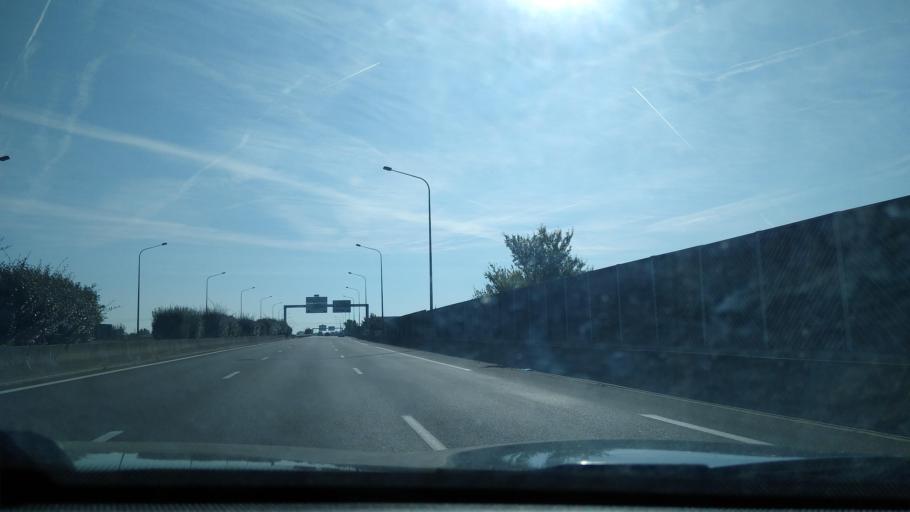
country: FR
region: Midi-Pyrenees
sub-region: Departement de la Haute-Garonne
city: Colomiers
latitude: 43.6041
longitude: 1.3671
